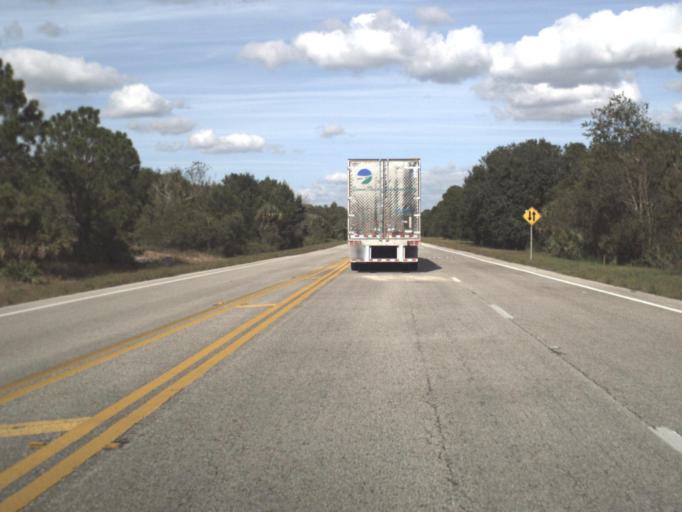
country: US
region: Florida
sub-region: Brevard County
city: Port Saint John
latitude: 28.5191
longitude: -80.8267
